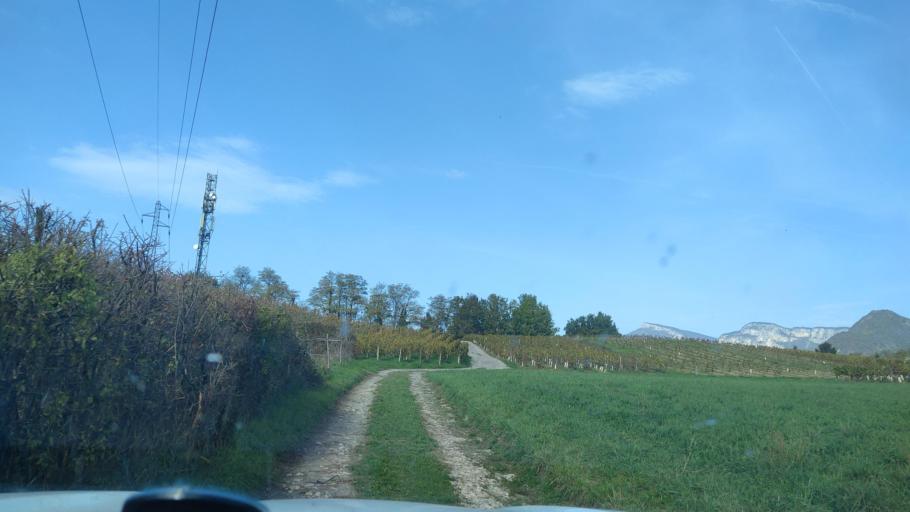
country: FR
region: Rhone-Alpes
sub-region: Departement de la Savoie
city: Les Marches
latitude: 45.5103
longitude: 5.9972
